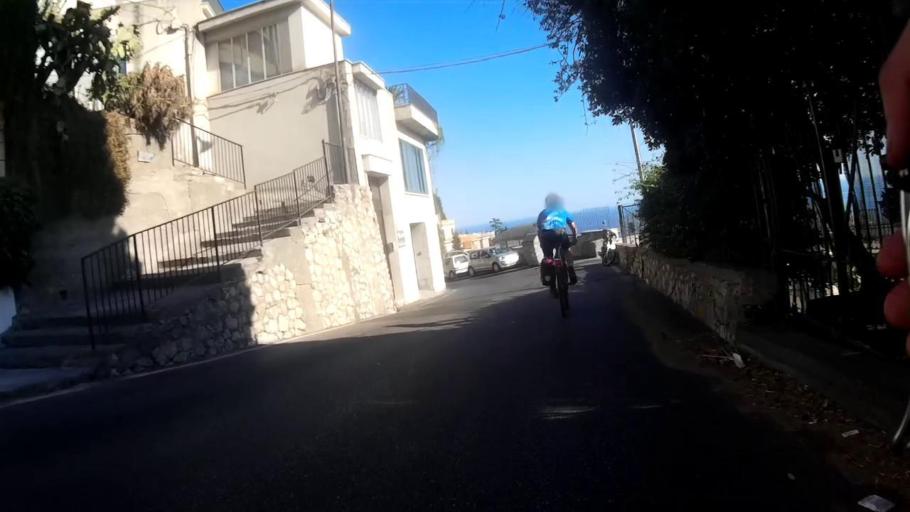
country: IT
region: Sicily
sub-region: Messina
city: Castelmola
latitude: 37.8546
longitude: 15.2819
